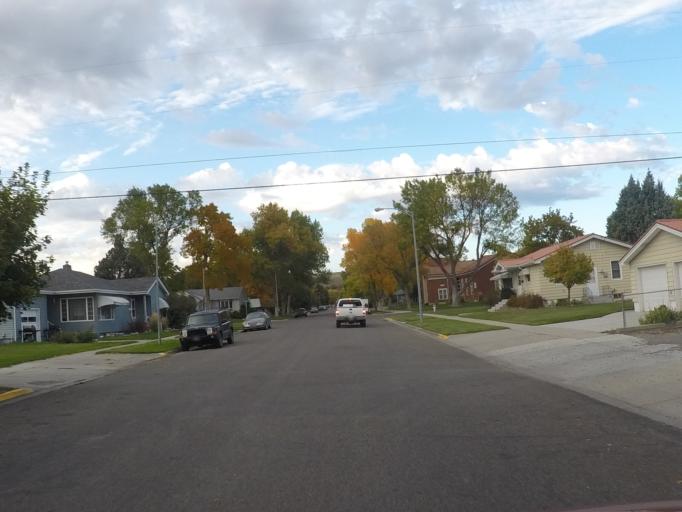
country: US
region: Montana
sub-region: Yellowstone County
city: Billings
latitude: 45.7863
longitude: -108.5306
